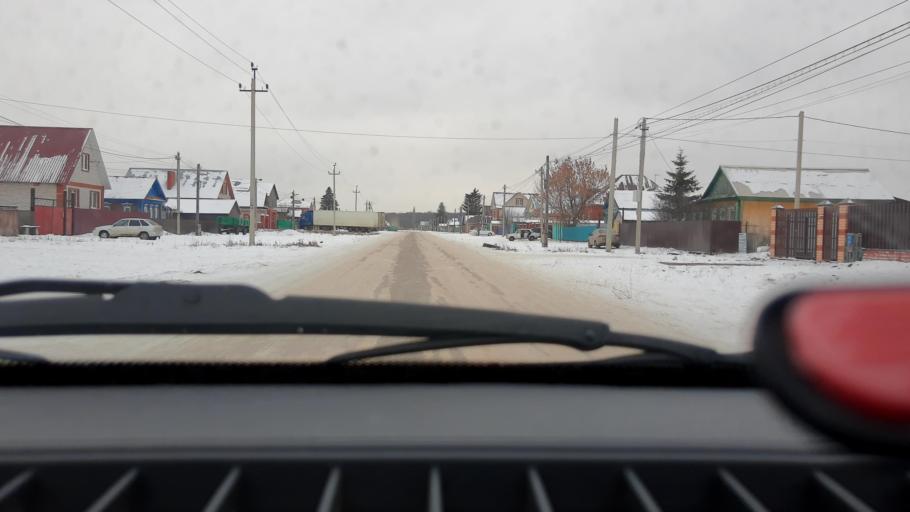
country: RU
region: Bashkortostan
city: Mikhaylovka
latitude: 54.7758
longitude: 55.8307
